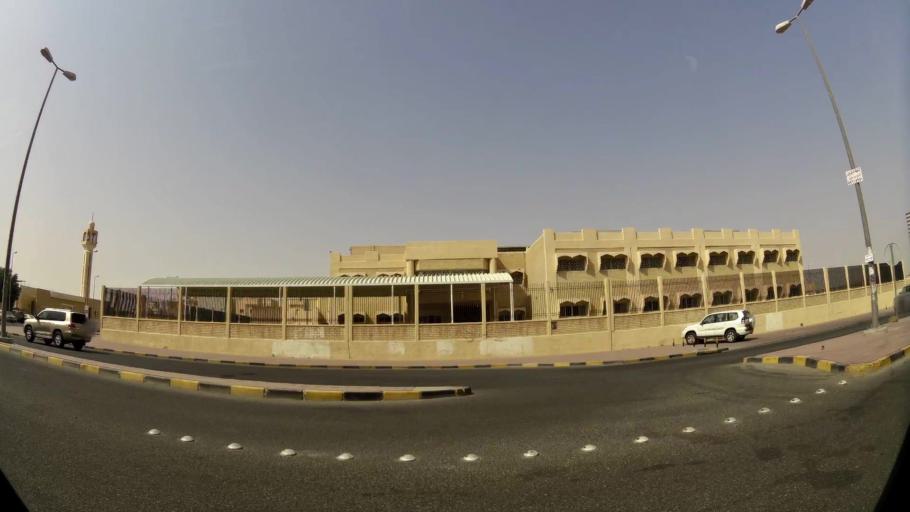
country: KW
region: Muhafazat al Jahra'
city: Al Jahra'
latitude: 29.3094
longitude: 47.7019
